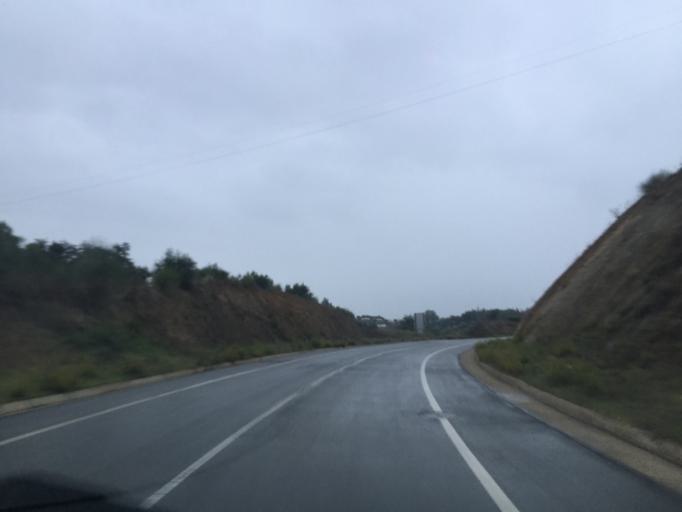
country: PT
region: Portalegre
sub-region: Avis
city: Avis
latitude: 39.0610
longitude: -7.8961
